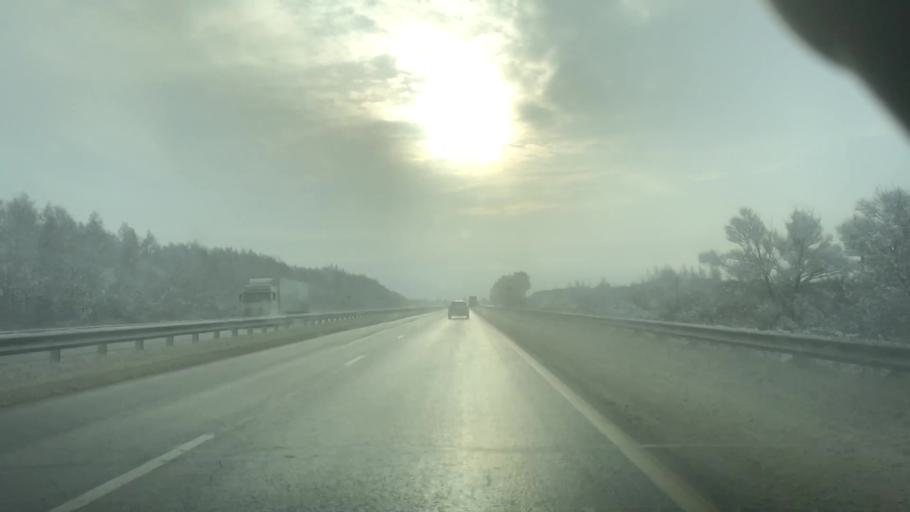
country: RU
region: Tula
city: Venev
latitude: 54.2888
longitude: 38.1587
